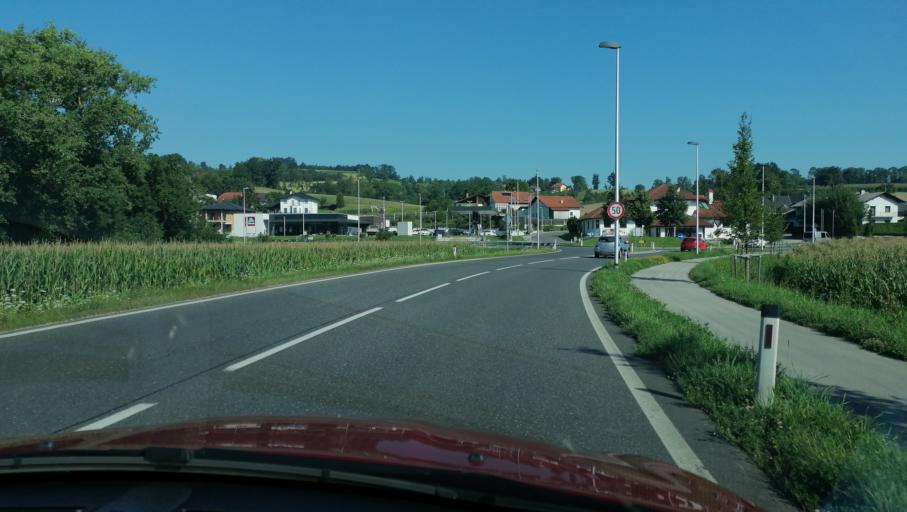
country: AT
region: Upper Austria
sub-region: Politischer Bezirk Grieskirchen
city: Bad Schallerbach
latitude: 48.2373
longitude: 13.9581
